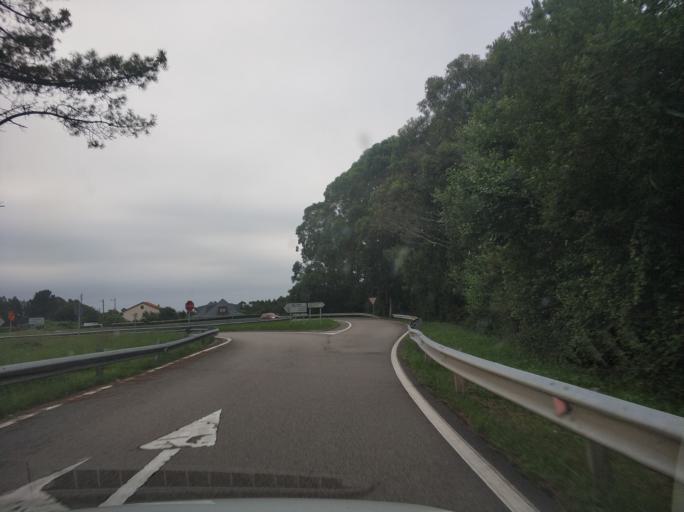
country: ES
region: Asturias
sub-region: Province of Asturias
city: Cudillero
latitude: 43.5608
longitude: -6.1769
